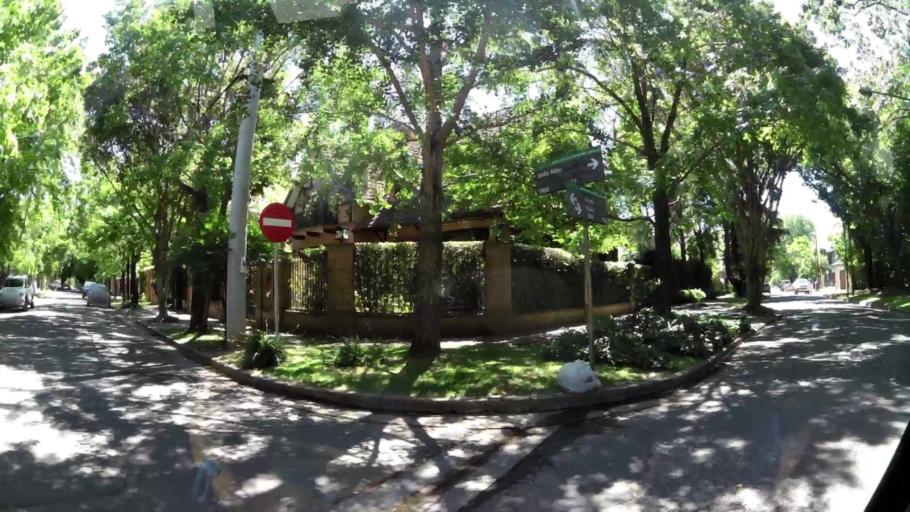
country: AR
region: Buenos Aires
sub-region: Partido de San Isidro
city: San Isidro
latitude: -34.4796
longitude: -58.4877
